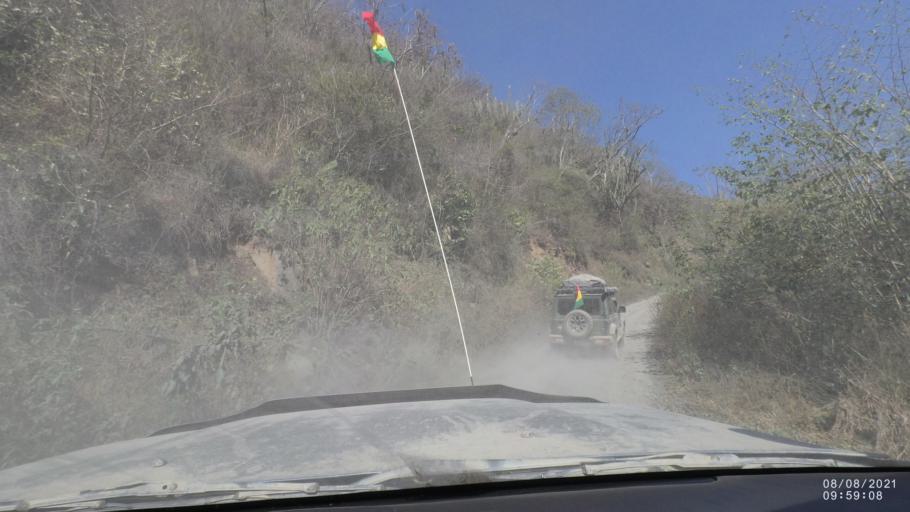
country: BO
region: La Paz
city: Quime
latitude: -16.6457
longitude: -66.7226
